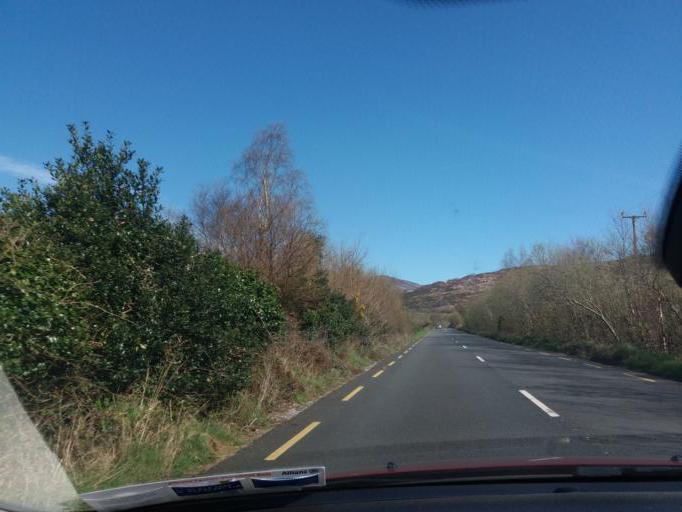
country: IE
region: Munster
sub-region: Ciarrai
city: Cill Airne
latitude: 51.9328
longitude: -9.3829
